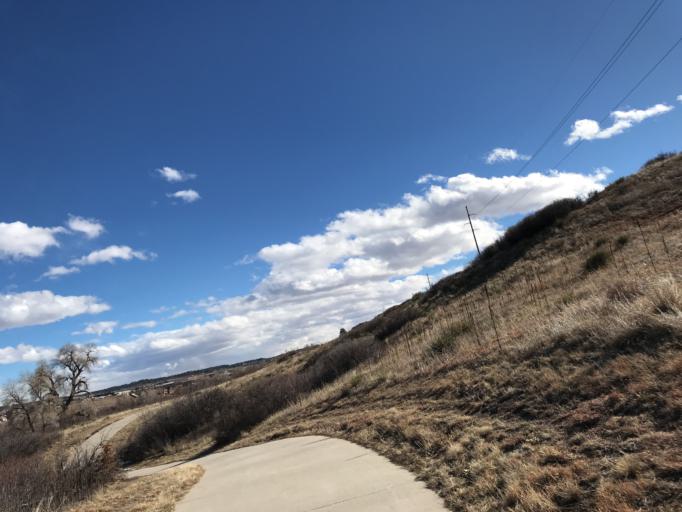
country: US
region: Colorado
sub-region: Douglas County
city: Castle Pines
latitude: 39.4126
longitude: -104.8867
